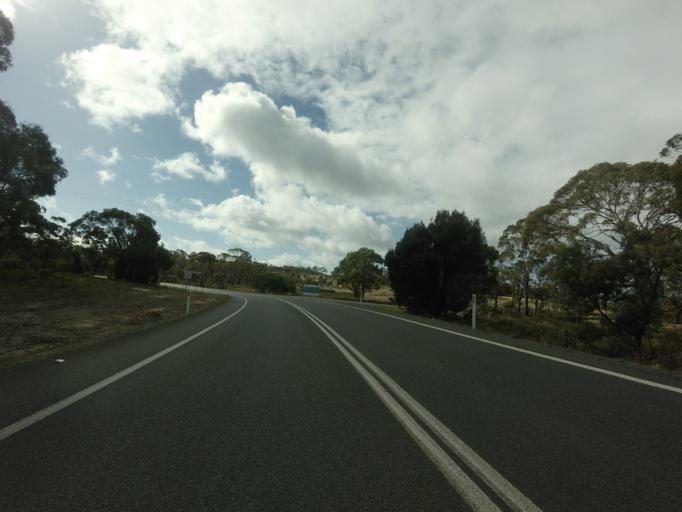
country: AU
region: Tasmania
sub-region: Sorell
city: Sorell
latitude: -42.5394
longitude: 147.8969
